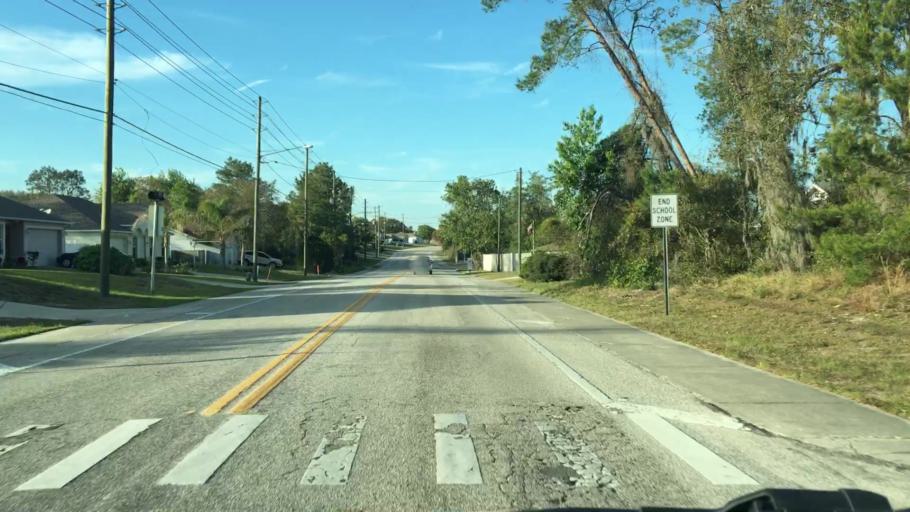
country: US
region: Florida
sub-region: Volusia County
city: Lake Helen
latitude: 28.9348
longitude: -81.2234
